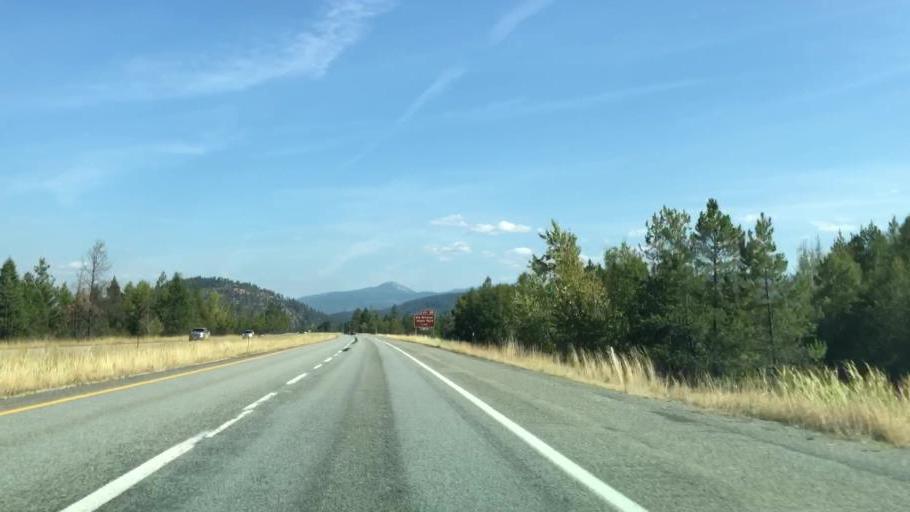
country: US
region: Idaho
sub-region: Shoshone County
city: Pinehurst
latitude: 47.5569
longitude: -116.3841
